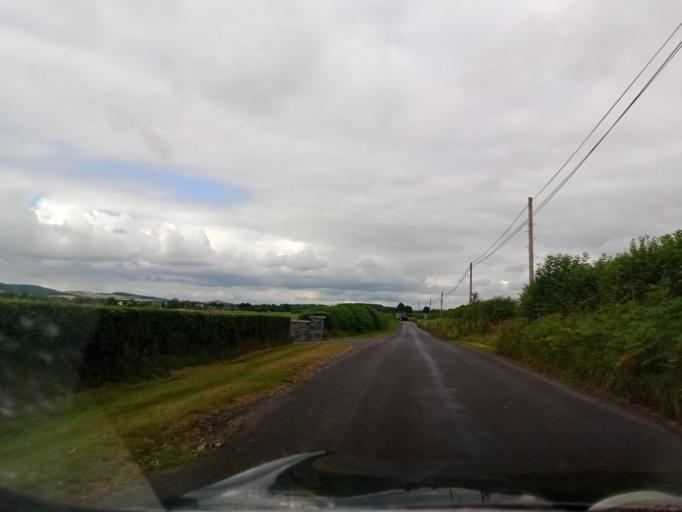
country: IE
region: Leinster
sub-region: Laois
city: Stradbally
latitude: 52.9853
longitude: -7.1824
